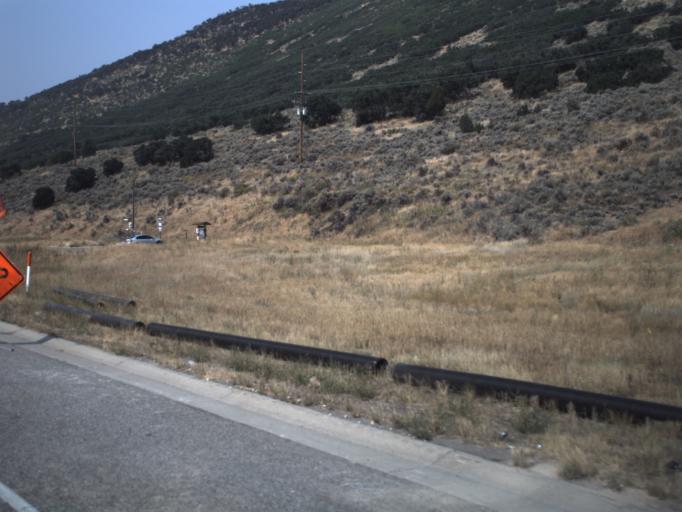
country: US
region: Utah
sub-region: Summit County
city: Snyderville
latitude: 40.6776
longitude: -111.5246
